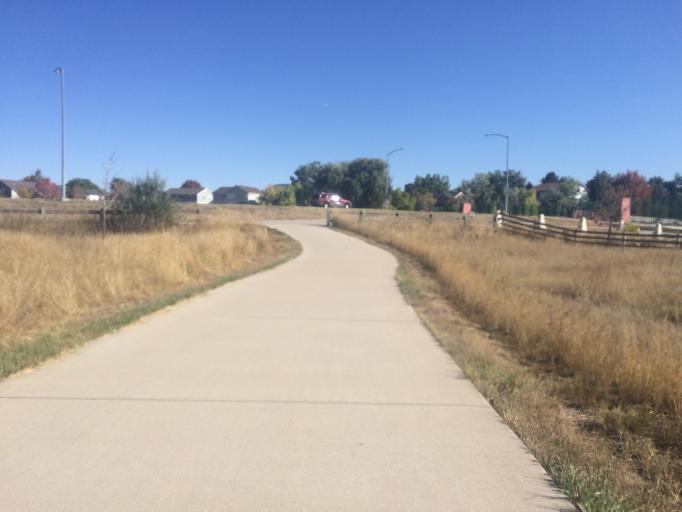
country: US
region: Colorado
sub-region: Broomfield County
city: Broomfield
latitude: 39.8756
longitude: -105.0821
